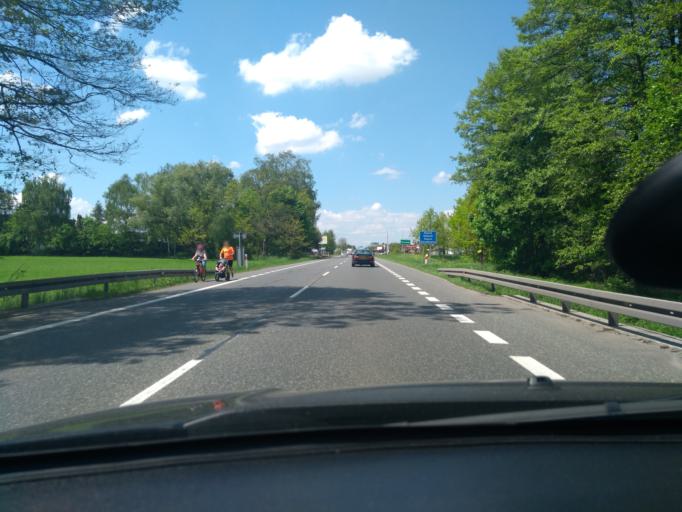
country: PL
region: Silesian Voivodeship
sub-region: Powiat gliwicki
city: Paniowki
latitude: 50.2291
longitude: 18.8017
